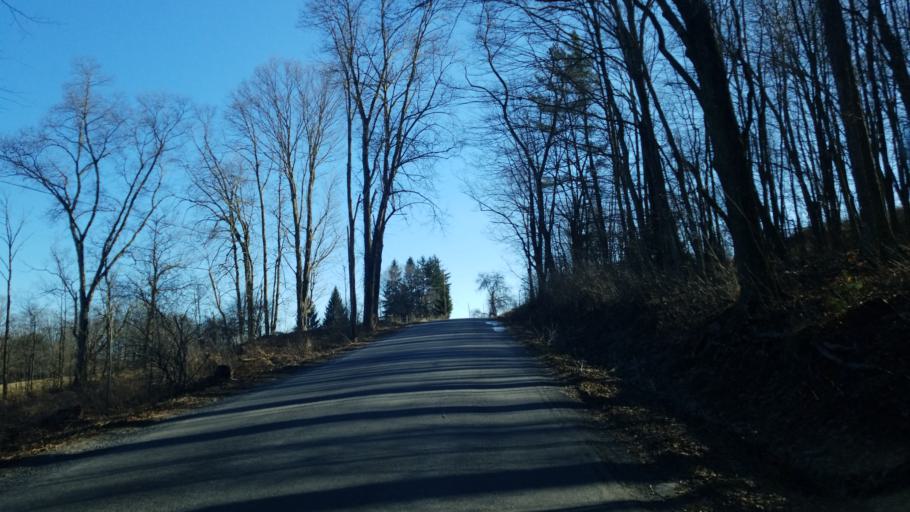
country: US
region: Pennsylvania
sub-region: Jefferson County
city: Sykesville
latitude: 41.0456
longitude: -78.7861
